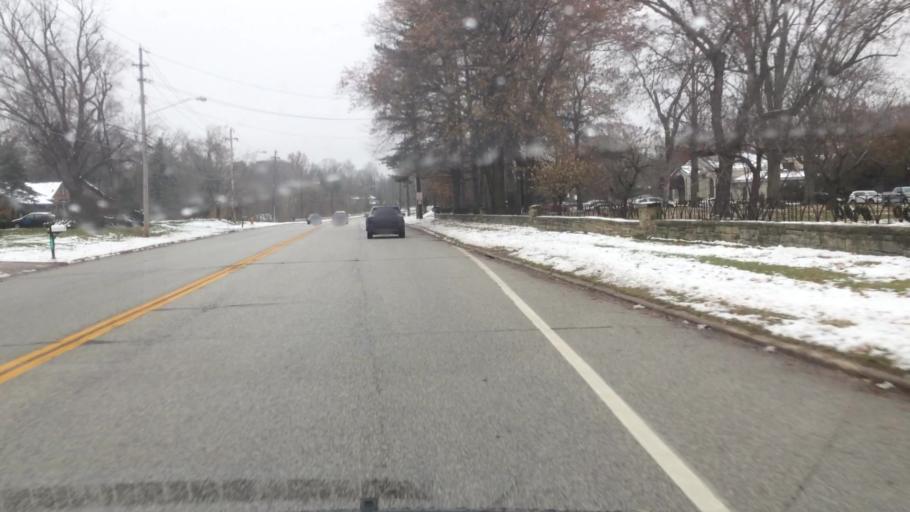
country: US
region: Ohio
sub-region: Cuyahoga County
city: North Olmsted
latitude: 41.4001
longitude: -81.9044
